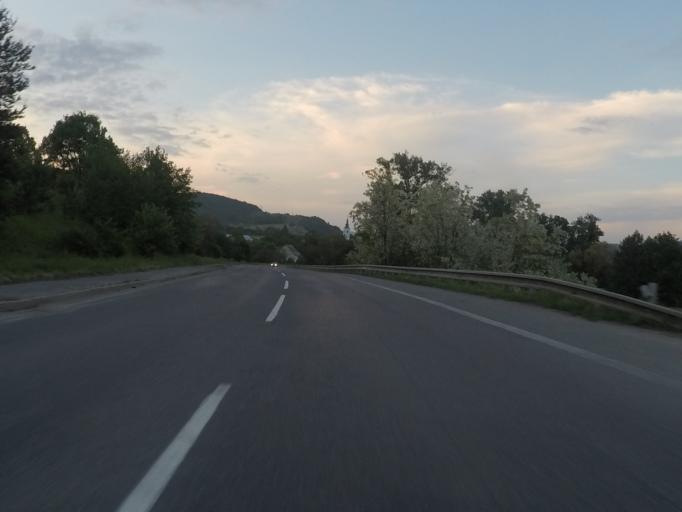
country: SK
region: Banskobystricky
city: Rimavska Sobota
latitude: 48.5046
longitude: 19.9377
